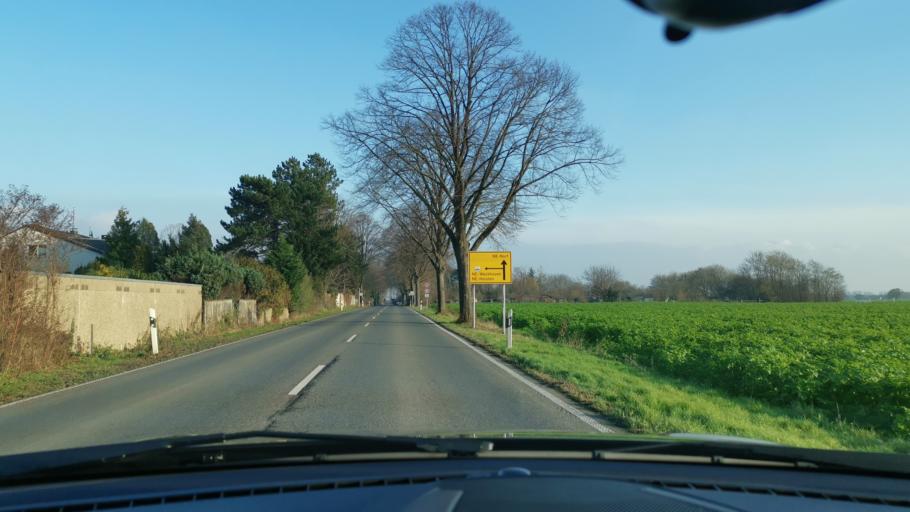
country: DE
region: North Rhine-Westphalia
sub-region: Regierungsbezirk Dusseldorf
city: Neubrueck
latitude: 51.1395
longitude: 6.6963
